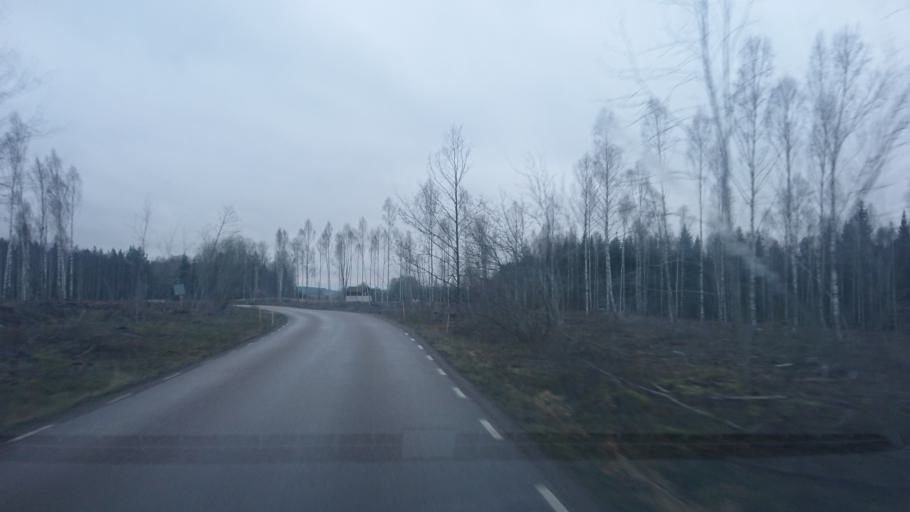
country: SE
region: Uppsala
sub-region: Osthammars Kommun
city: Bjorklinge
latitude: 60.0235
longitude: 17.5743
